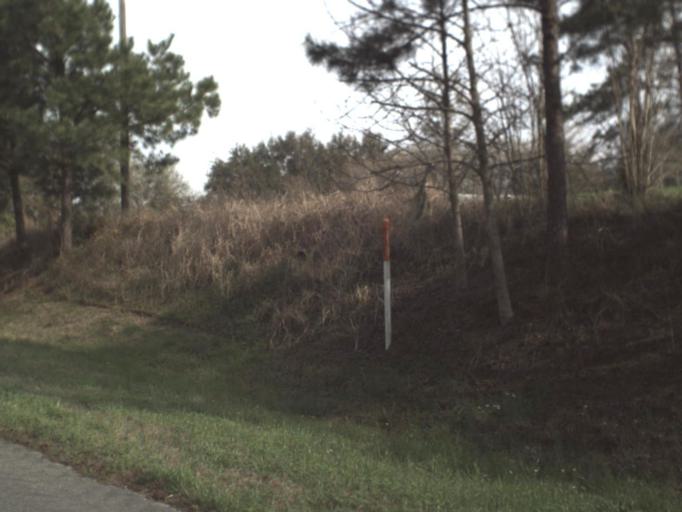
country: US
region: Florida
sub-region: Jefferson County
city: Monticello
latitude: 30.5342
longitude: -83.9458
